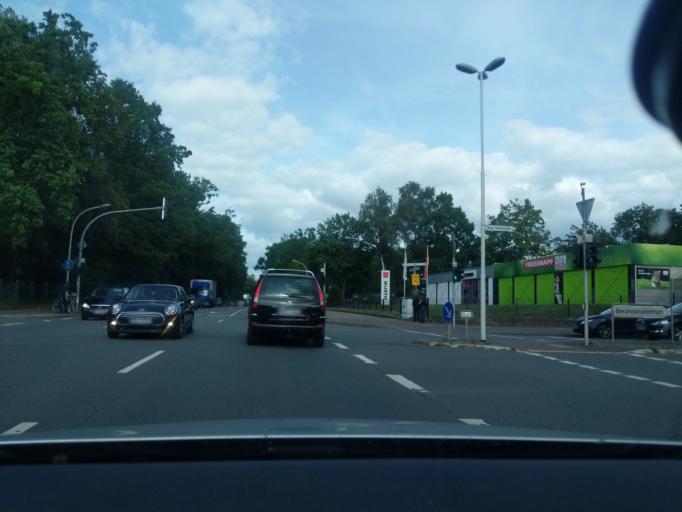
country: DE
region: Lower Saxony
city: Verden
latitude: 52.9525
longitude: 9.2375
